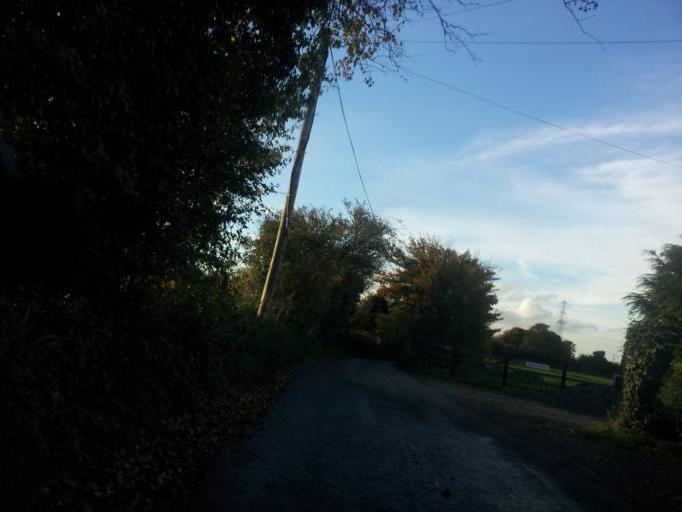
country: GB
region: England
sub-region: Kent
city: Newington
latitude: 51.3605
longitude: 0.6650
